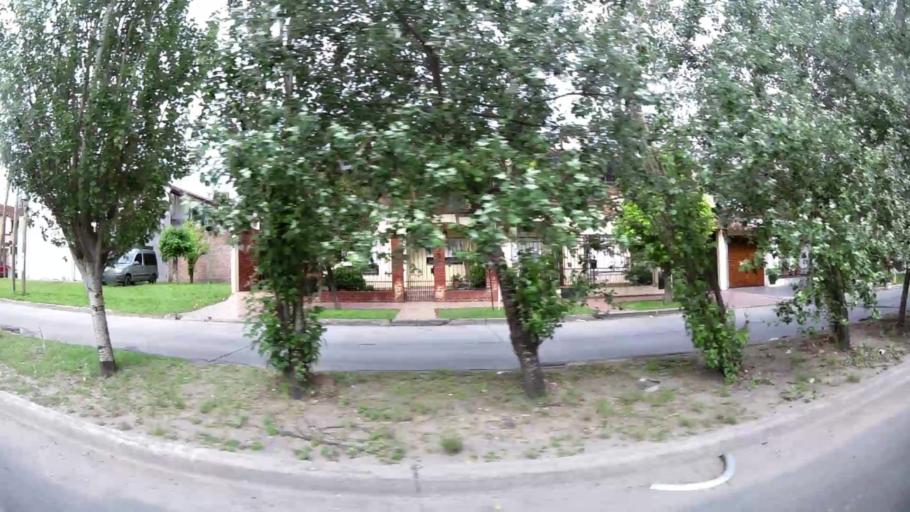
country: AR
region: Buenos Aires
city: San Justo
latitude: -34.7182
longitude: -58.5351
